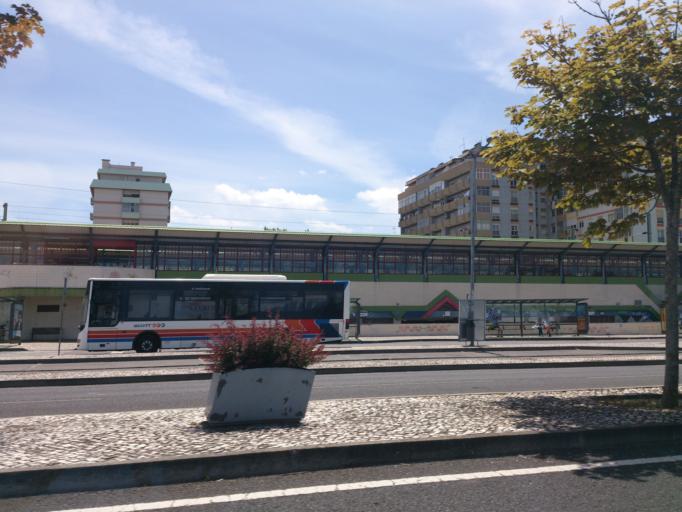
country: PT
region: Lisbon
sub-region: Sintra
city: Sintra
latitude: 38.8028
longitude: -9.3765
